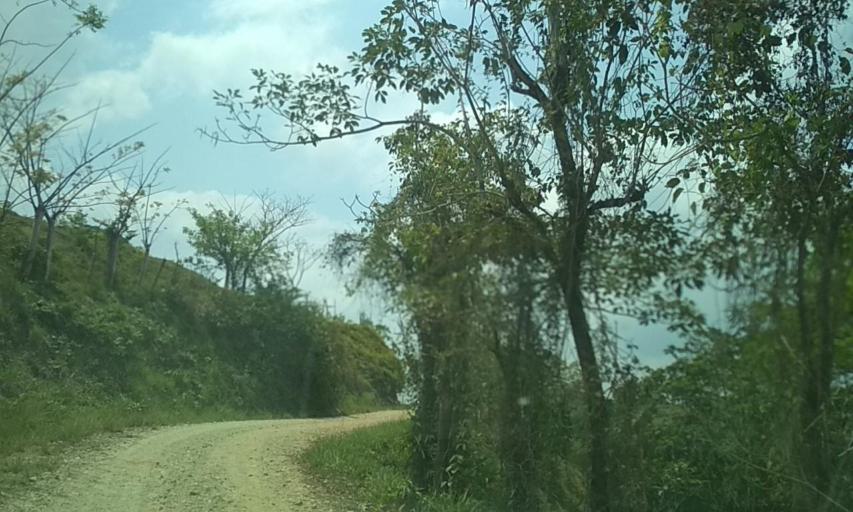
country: MX
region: Tabasco
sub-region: Huimanguillo
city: Francisco Rueda
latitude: 17.6136
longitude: -93.8131
